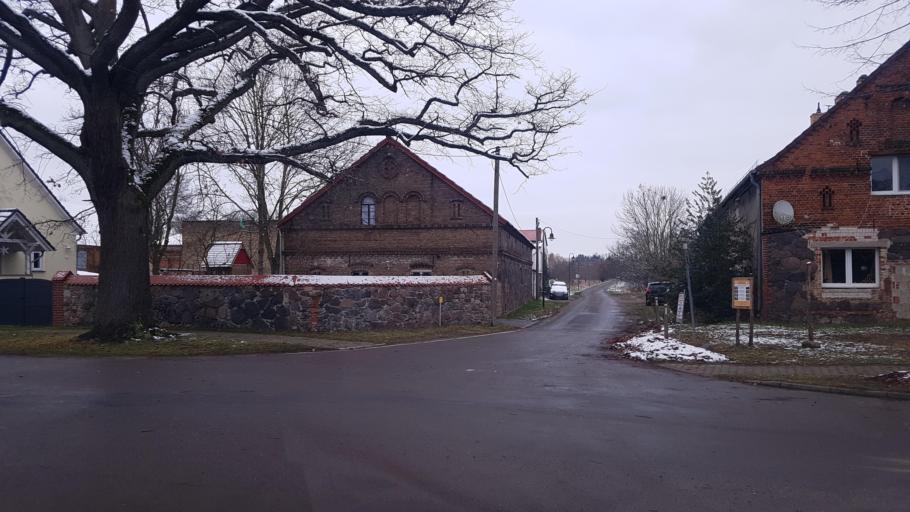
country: DE
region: Brandenburg
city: Rehfelde
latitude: 52.5206
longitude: 13.9451
